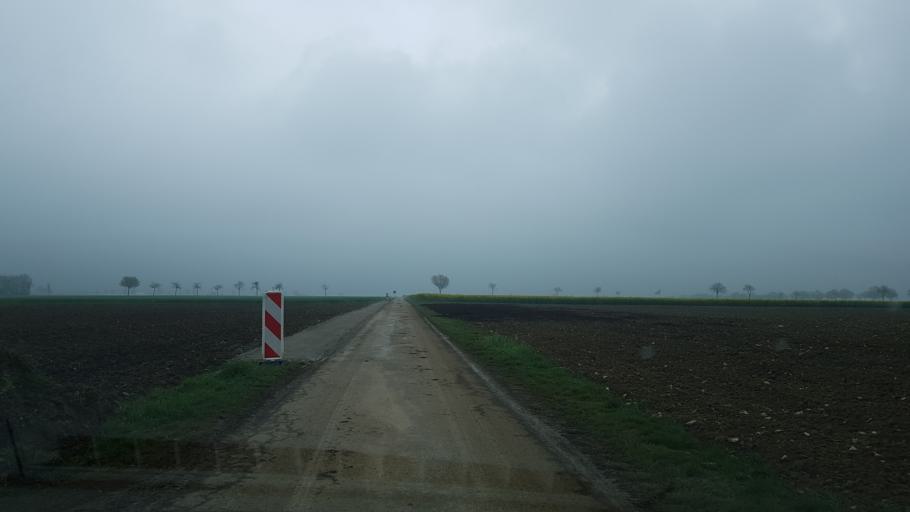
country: DE
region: North Rhine-Westphalia
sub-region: Regierungsbezirk Detmold
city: Paderborn
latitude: 51.6195
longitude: 8.7338
